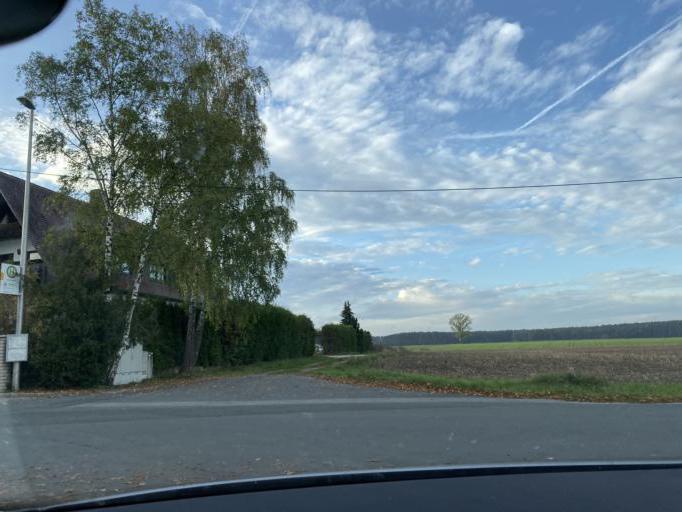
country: DE
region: Bavaria
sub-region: Regierungsbezirk Mittelfranken
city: Puschendorf
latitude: 49.5454
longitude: 10.8331
